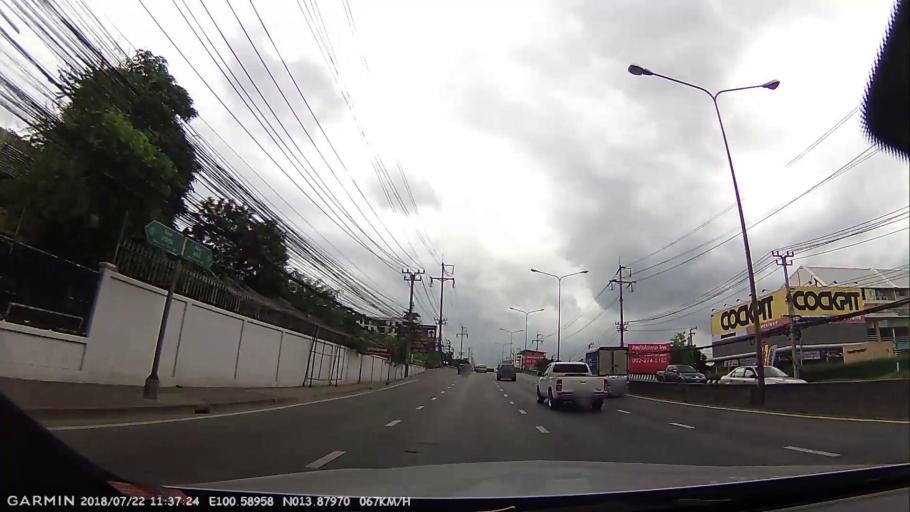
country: TH
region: Bangkok
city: Lak Si
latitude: 13.8798
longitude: 100.5895
